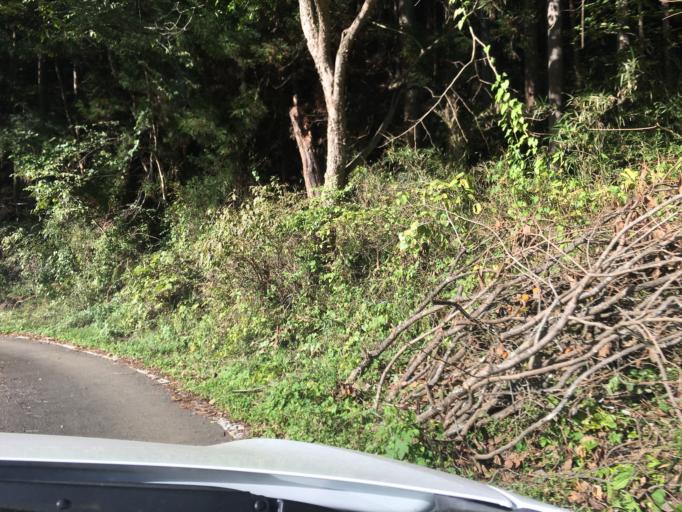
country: JP
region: Fukushima
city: Ishikawa
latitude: 37.1630
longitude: 140.5082
